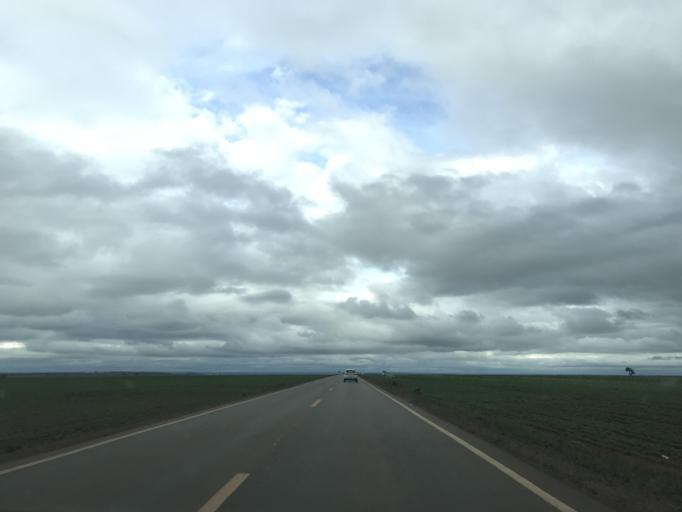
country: BR
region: Goias
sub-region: Luziania
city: Luziania
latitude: -16.5008
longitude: -48.2100
